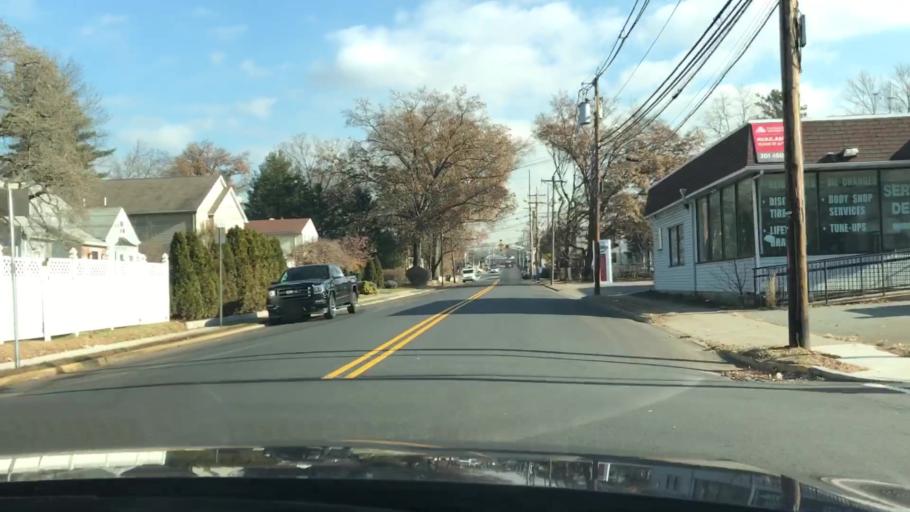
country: US
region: New Jersey
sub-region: Bergen County
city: Bergenfield
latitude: 40.9292
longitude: -74.0009
